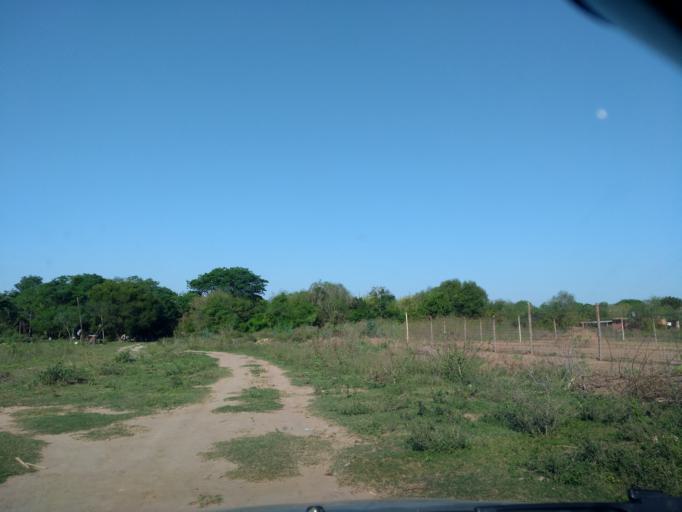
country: AR
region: Chaco
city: Fontana
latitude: -27.4111
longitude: -59.0120
